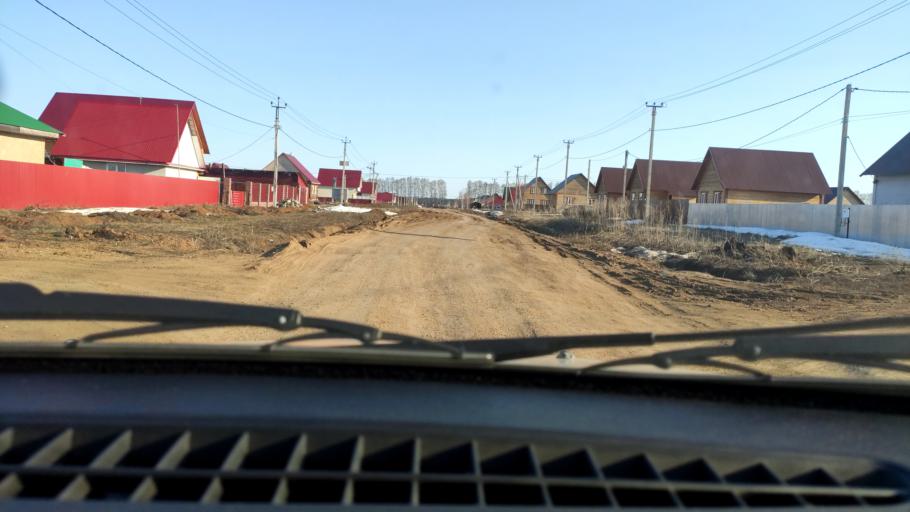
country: RU
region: Bashkortostan
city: Iglino
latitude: 54.8215
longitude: 56.4414
